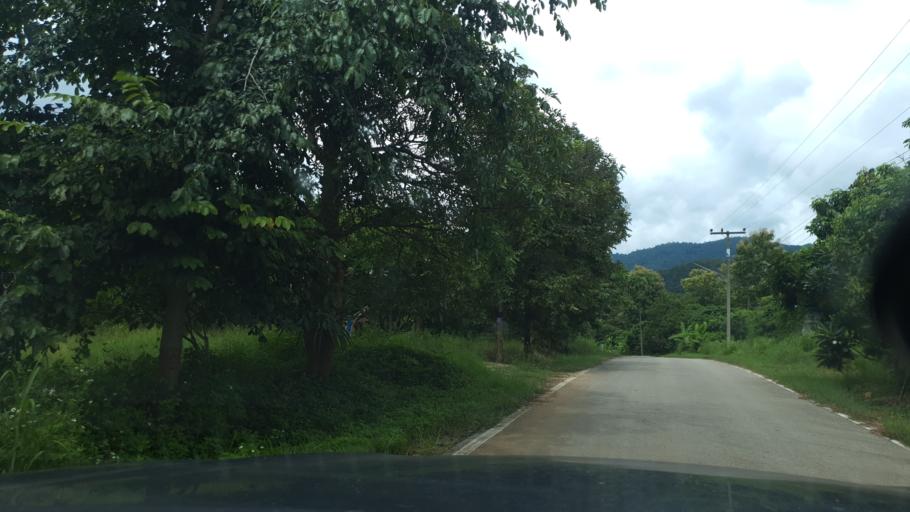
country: TH
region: Lampang
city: Hang Chat
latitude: 18.4236
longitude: 99.2643
